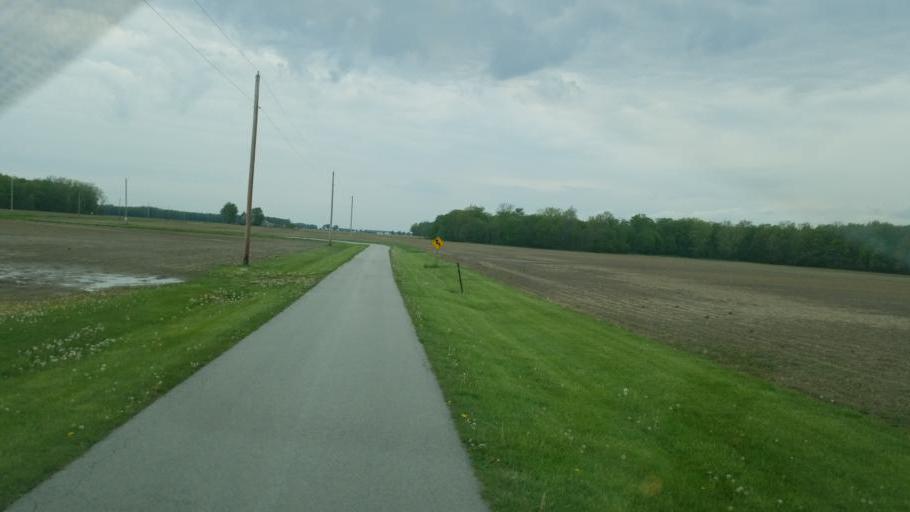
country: US
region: Ohio
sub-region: Huron County
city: Willard
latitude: 41.0197
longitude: -82.8457
